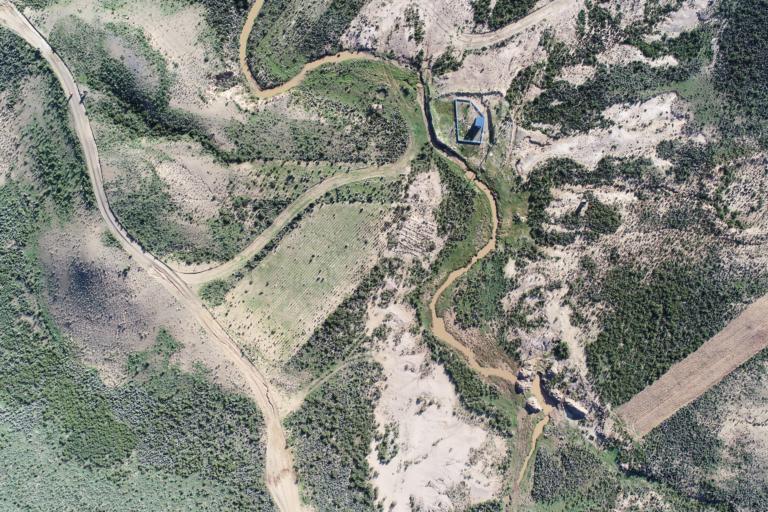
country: BO
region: La Paz
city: Curahuara de Carangas
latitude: -17.3007
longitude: -68.5184
